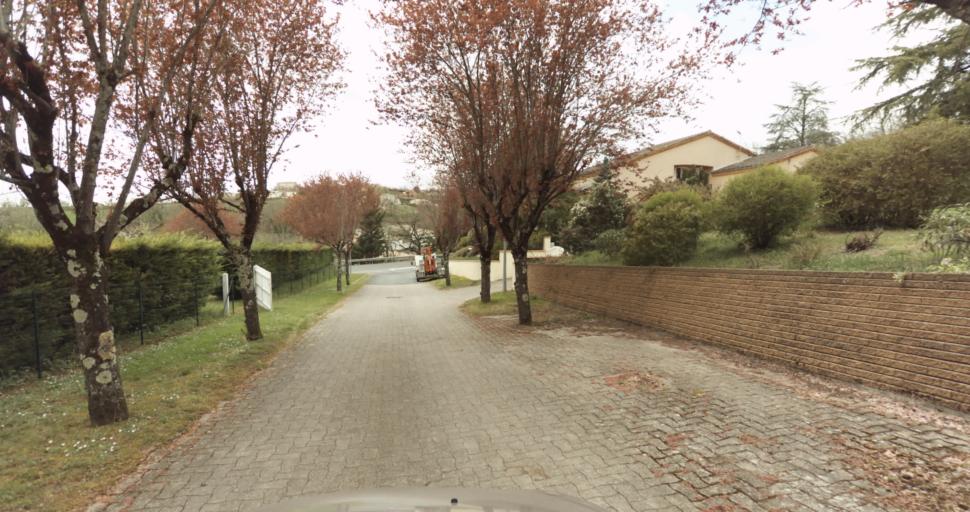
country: FR
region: Midi-Pyrenees
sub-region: Departement du Tarn
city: Puygouzon
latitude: 43.8996
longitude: 2.1737
